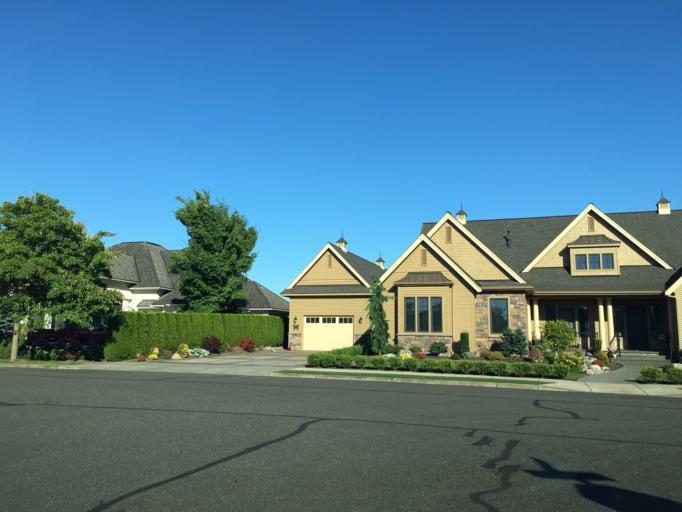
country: US
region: Washington
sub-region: Whatcom County
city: Lynden
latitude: 48.9599
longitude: -122.4563
